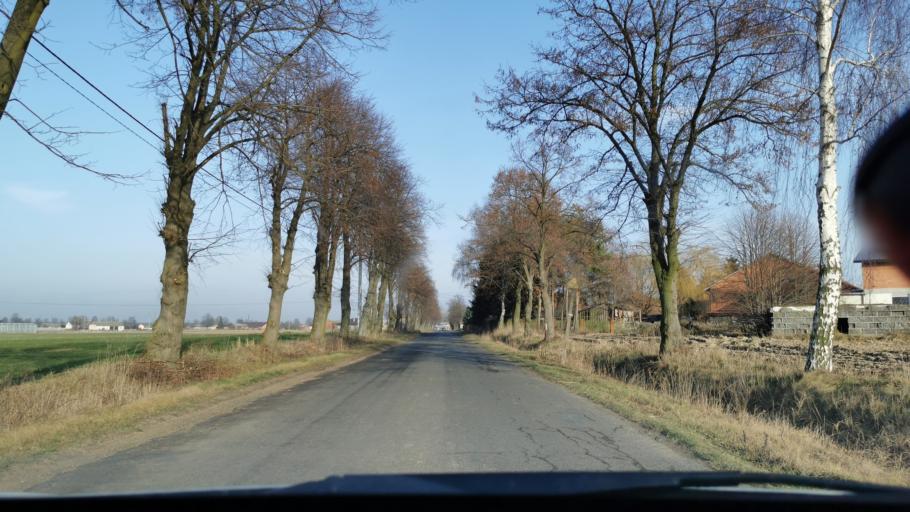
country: PL
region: Greater Poland Voivodeship
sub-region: Powiat kaliski
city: Opatowek
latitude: 51.6825
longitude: 18.3115
